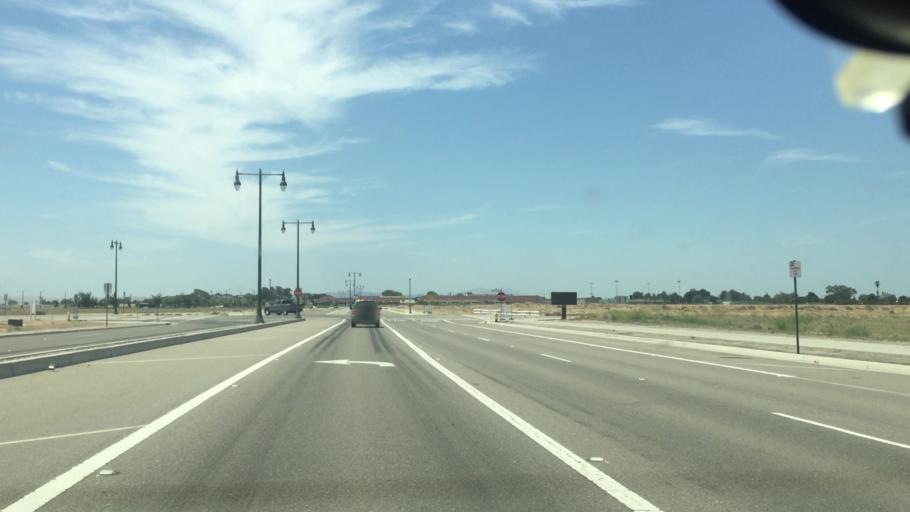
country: US
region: California
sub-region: San Joaquin County
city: Lathrop
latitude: 37.8263
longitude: -121.2942
